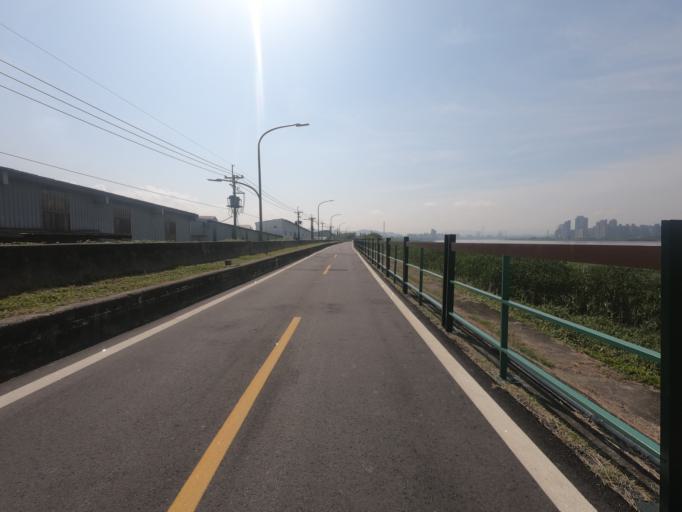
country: TW
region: Taipei
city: Taipei
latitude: 25.1037
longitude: 121.4811
